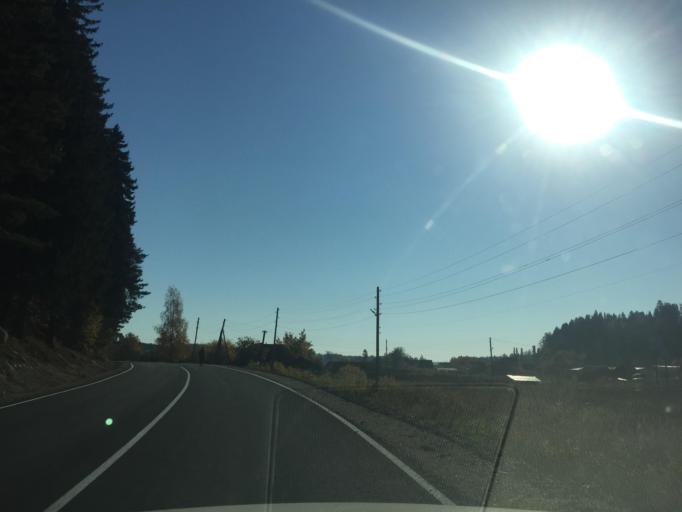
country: RU
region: Leningrad
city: Kuznechnoye
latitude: 61.3034
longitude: 29.8824
